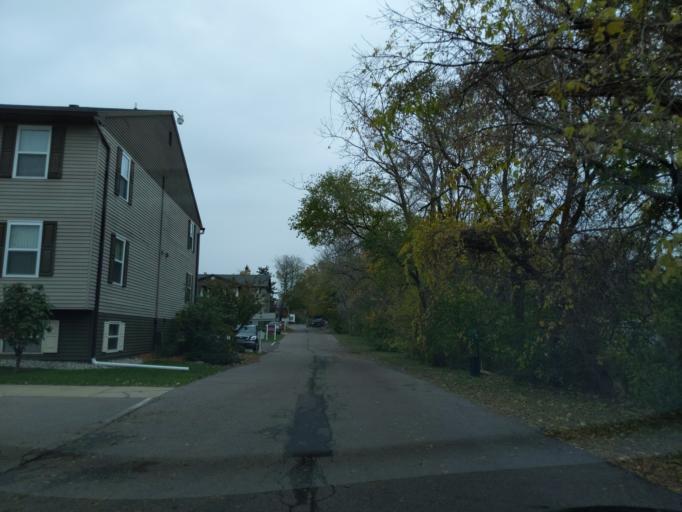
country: US
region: Michigan
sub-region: Ingham County
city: Edgemont Park
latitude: 42.7105
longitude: -84.5948
